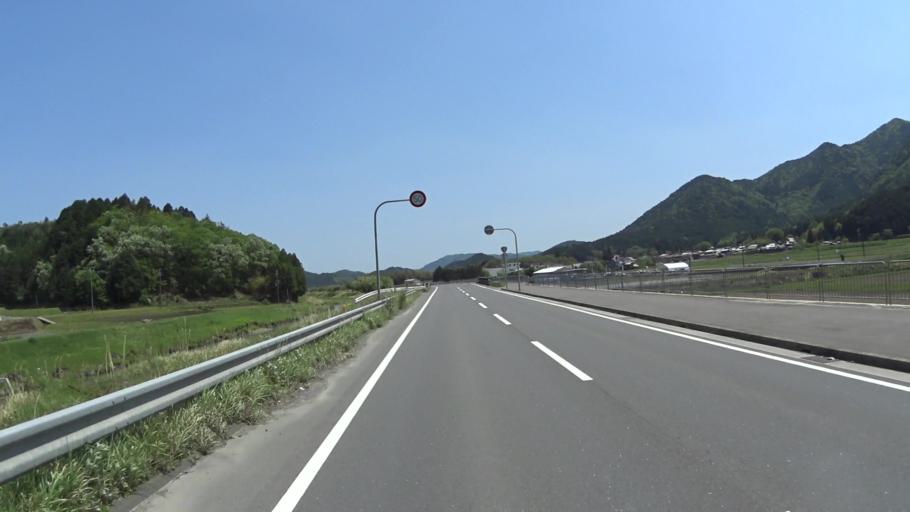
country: JP
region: Kyoto
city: Kameoka
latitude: 35.0567
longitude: 135.4647
